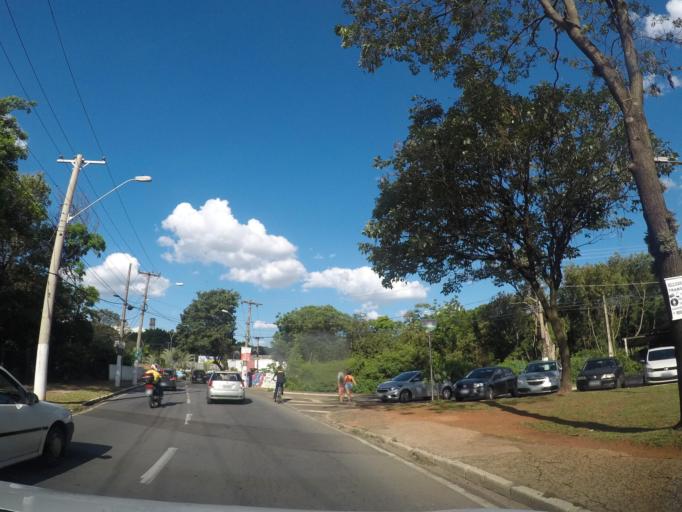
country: BR
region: Sao Paulo
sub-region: Sumare
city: Sumare
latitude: -22.8199
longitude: -47.2634
